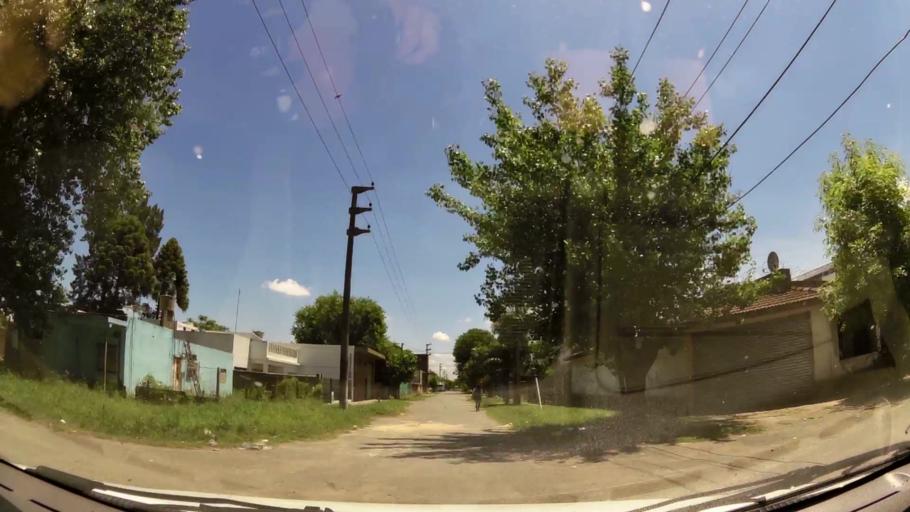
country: AR
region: Buenos Aires
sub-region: Partido de Merlo
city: Merlo
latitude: -34.6443
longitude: -58.7106
